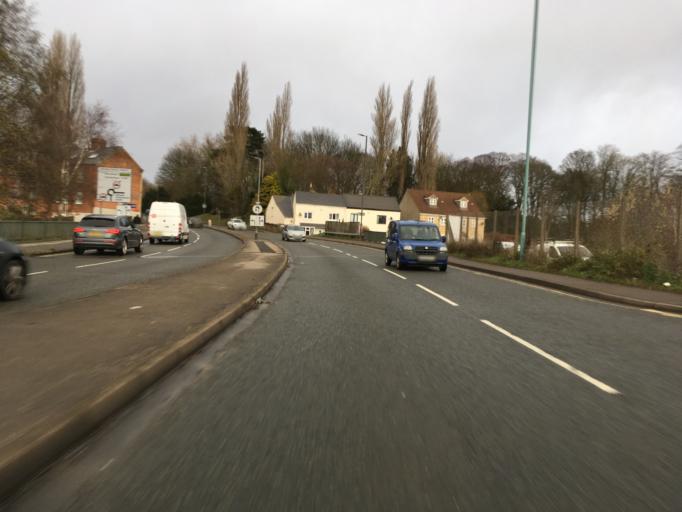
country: GB
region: England
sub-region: Gloucestershire
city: Stroud
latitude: 51.7419
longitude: -2.2394
